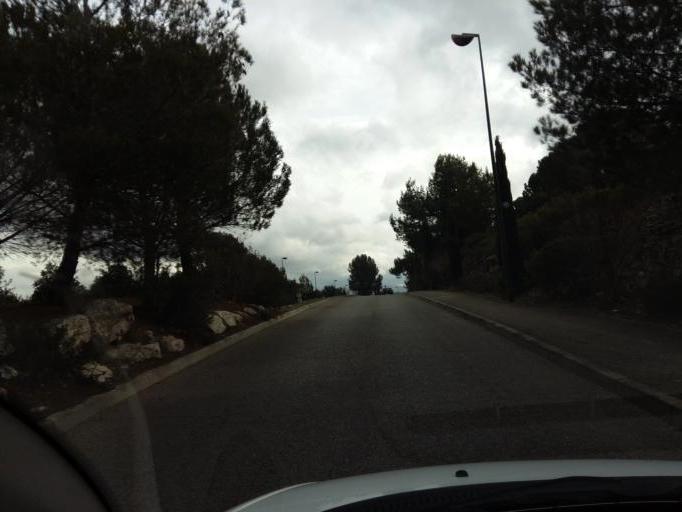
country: FR
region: Provence-Alpes-Cote d'Azur
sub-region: Departement des Bouches-du-Rhone
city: Cabries
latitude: 43.4892
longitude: 5.3576
